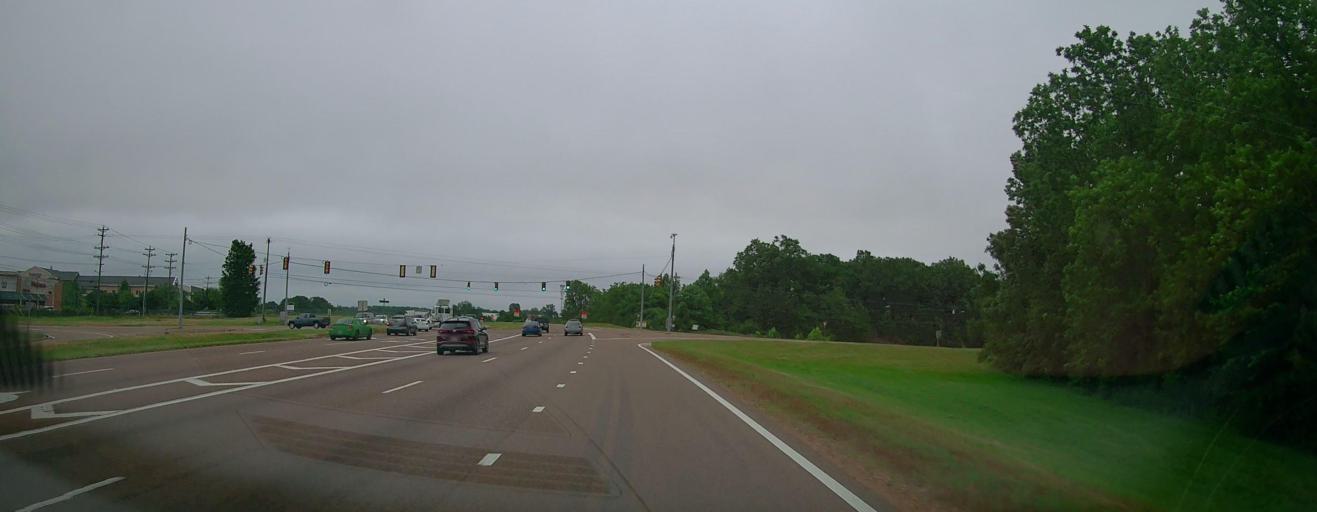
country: US
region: Mississippi
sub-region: De Soto County
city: Olive Branch
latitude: 34.9623
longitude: -89.7970
